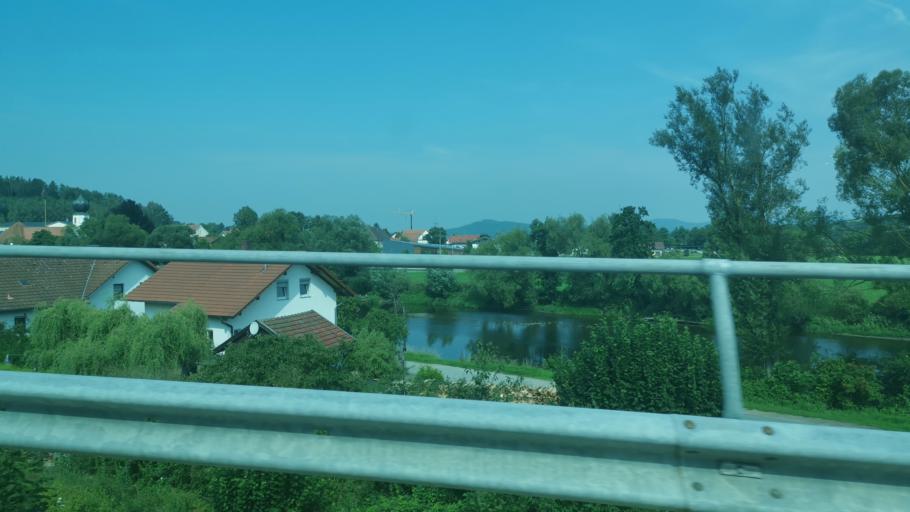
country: DE
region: Bavaria
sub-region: Upper Palatinate
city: Chamerau
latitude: 49.1978
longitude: 12.7498
